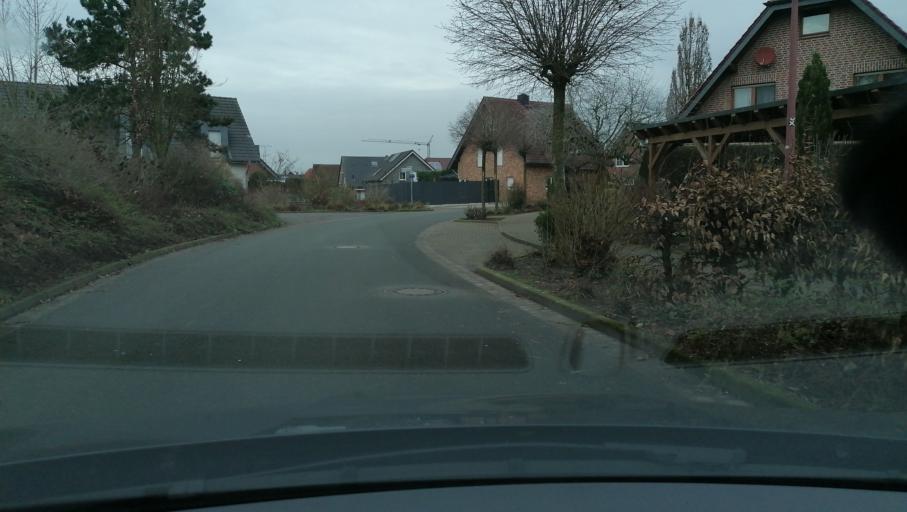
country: DE
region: North Rhine-Westphalia
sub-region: Regierungsbezirk Munster
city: Klein Reken
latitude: 51.7981
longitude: 7.0420
